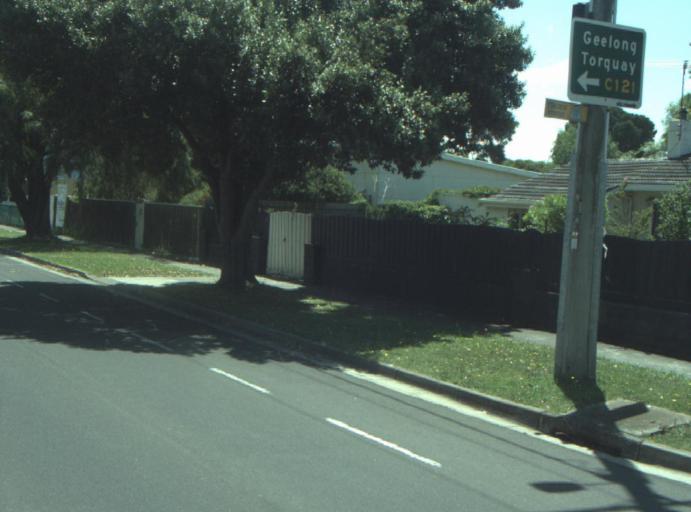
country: AU
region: Victoria
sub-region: Greater Geelong
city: Leopold
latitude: -38.2763
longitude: 144.4882
